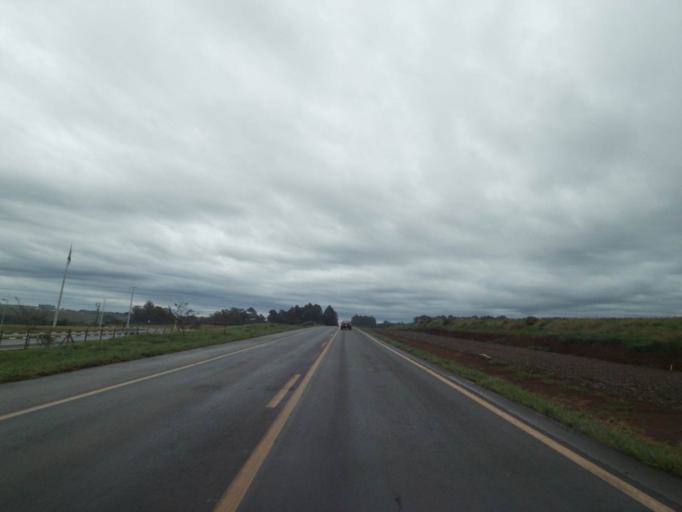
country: BR
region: Parana
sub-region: Toledo
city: Toledo
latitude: -24.6894
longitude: -53.7546
